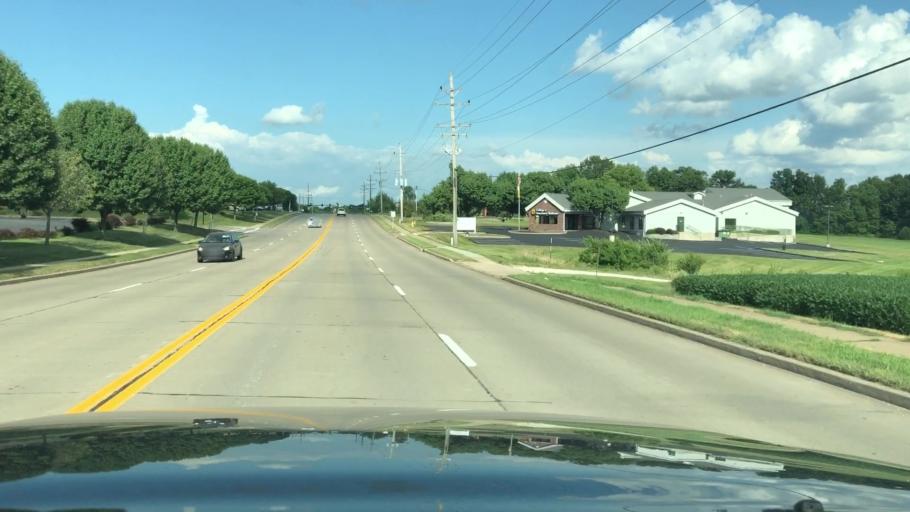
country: US
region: Missouri
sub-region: Saint Charles County
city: Wentzville
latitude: 38.8249
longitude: -90.8642
